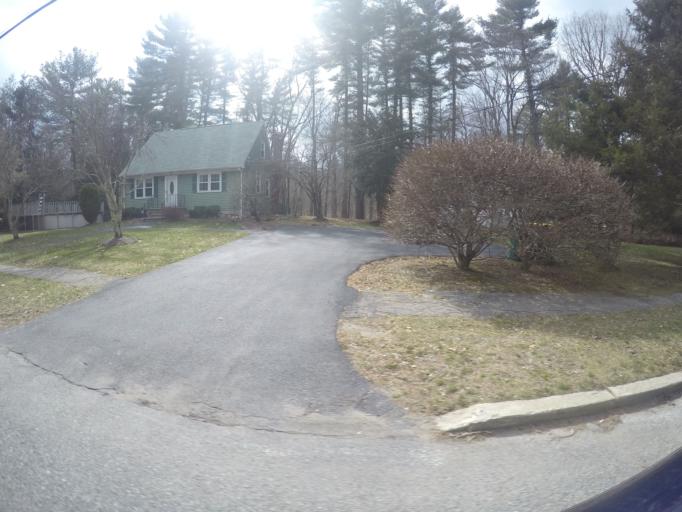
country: US
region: Massachusetts
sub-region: Bristol County
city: Easton
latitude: 42.0465
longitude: -71.1164
